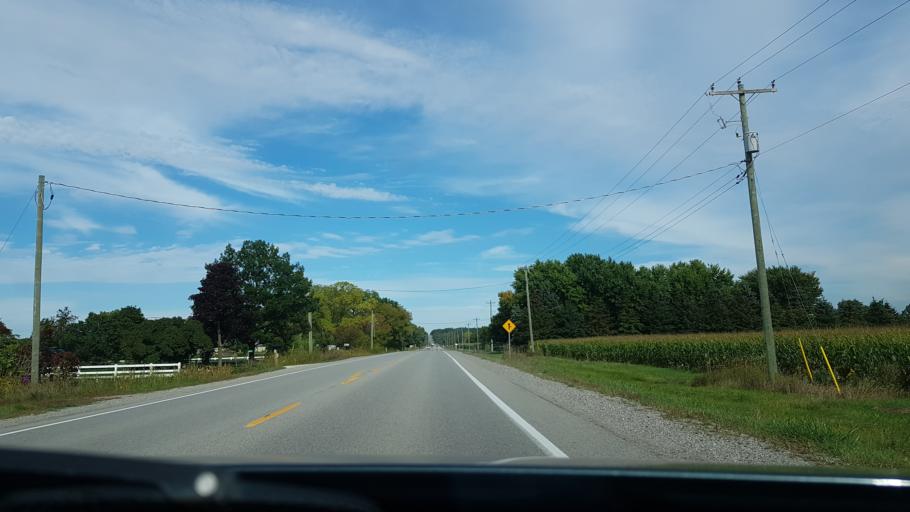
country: CA
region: Ontario
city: Angus
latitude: 44.4731
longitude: -79.8503
